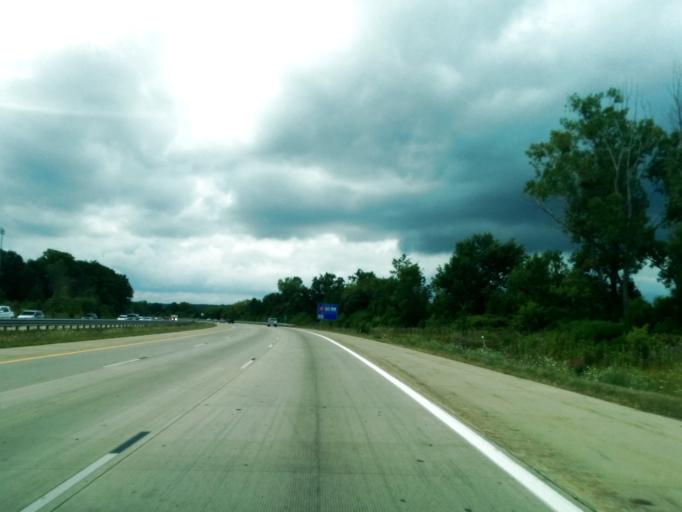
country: US
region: Michigan
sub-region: Oakland County
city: Rochester Hills
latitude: 42.6424
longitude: -83.1529
